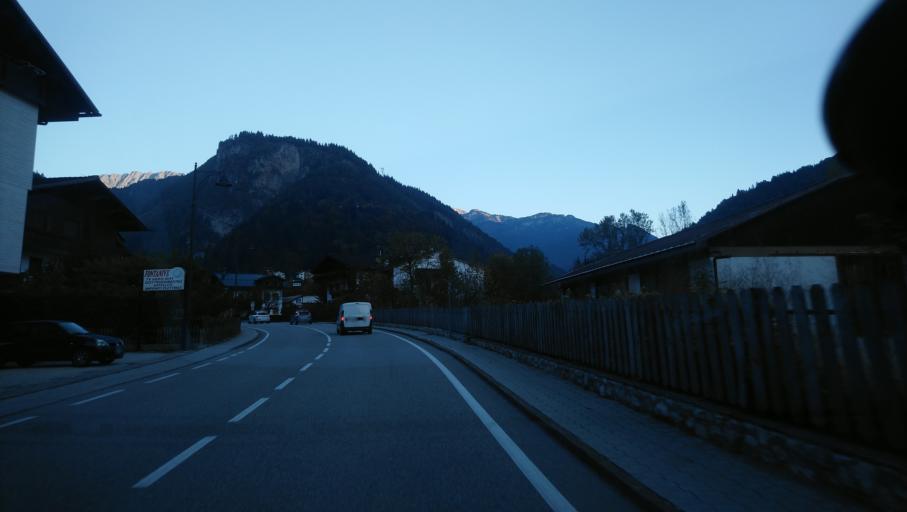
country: IT
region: Veneto
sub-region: Provincia di Belluno
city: Cencenighe Agordino
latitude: 46.3485
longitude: 11.9692
